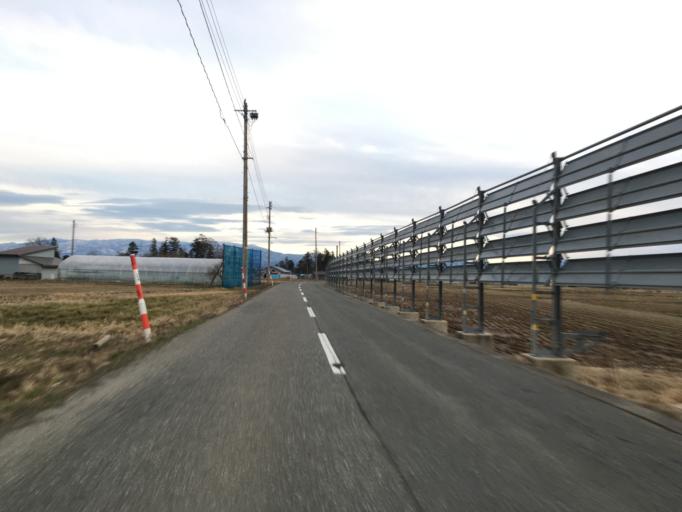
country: JP
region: Yamagata
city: Nagai
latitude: 38.0165
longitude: 140.0793
